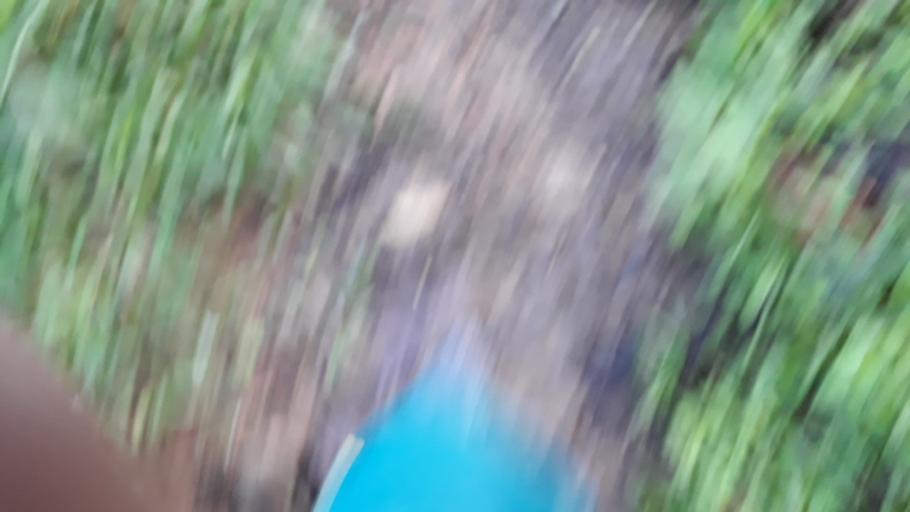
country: CO
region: Casanare
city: Nunchia
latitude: 5.6414
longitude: -72.4247
